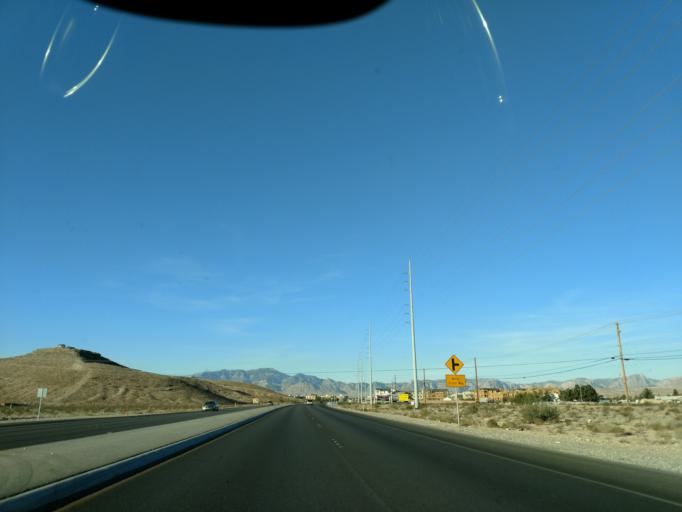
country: US
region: Nevada
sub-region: Clark County
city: Enterprise
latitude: 36.0210
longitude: -115.2516
